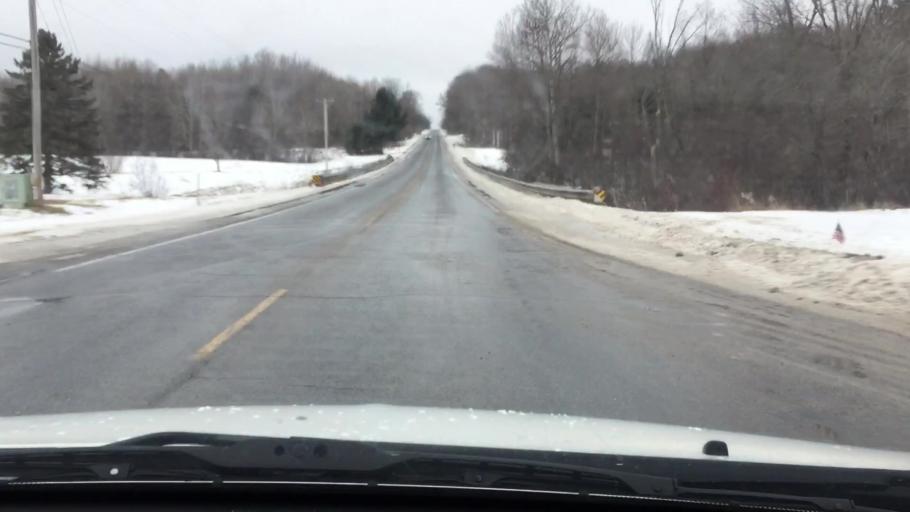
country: US
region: Michigan
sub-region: Wexford County
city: Cadillac
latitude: 44.1023
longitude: -85.4443
